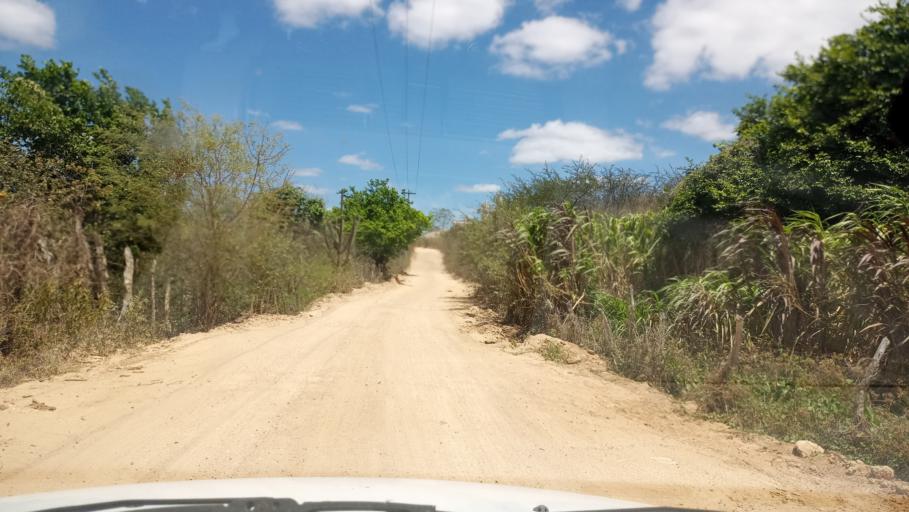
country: BR
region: Rio Grande do Norte
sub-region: Sao Paulo Do Potengi
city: Sao Paulo do Potengi
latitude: -5.7933
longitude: -35.9207
